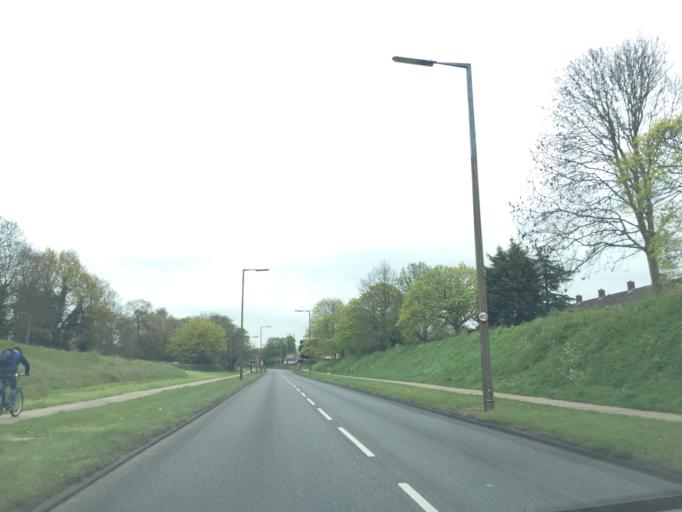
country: GB
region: England
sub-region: Essex
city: Harlow
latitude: 51.7693
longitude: 0.0820
